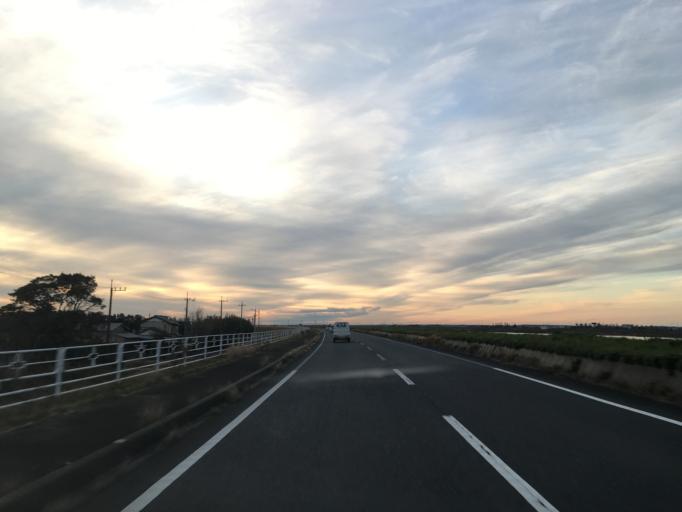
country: JP
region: Chiba
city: Katori-shi
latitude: 35.9155
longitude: 140.4620
